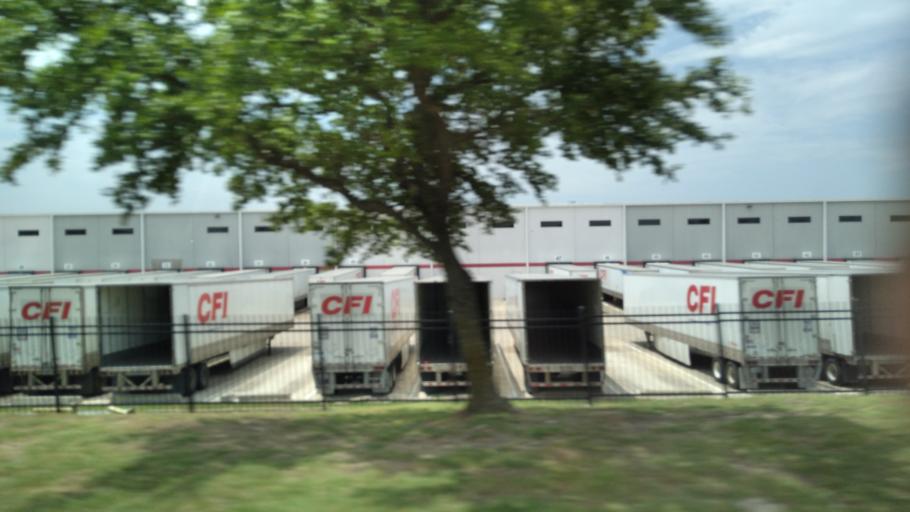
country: US
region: Texas
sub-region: McLennan County
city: Beverly Hills
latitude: 31.4881
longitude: -97.1595
